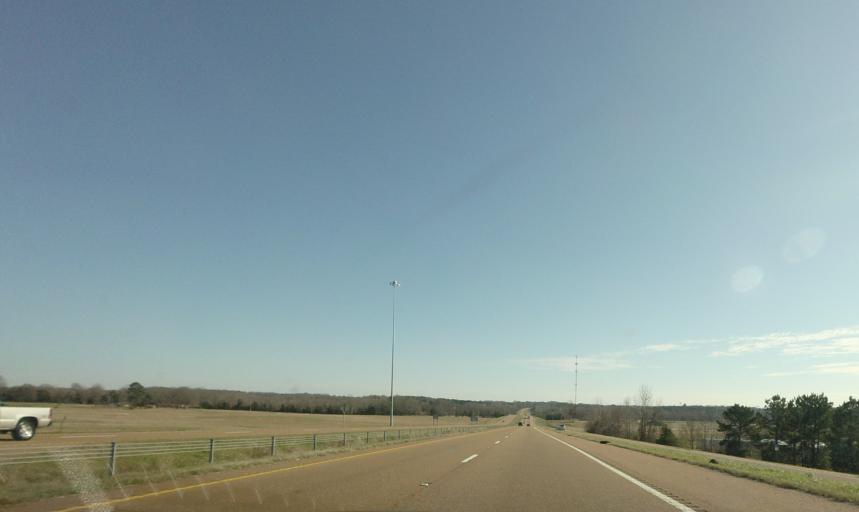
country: US
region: Mississippi
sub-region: Union County
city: New Albany
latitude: 34.4691
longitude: -89.0054
